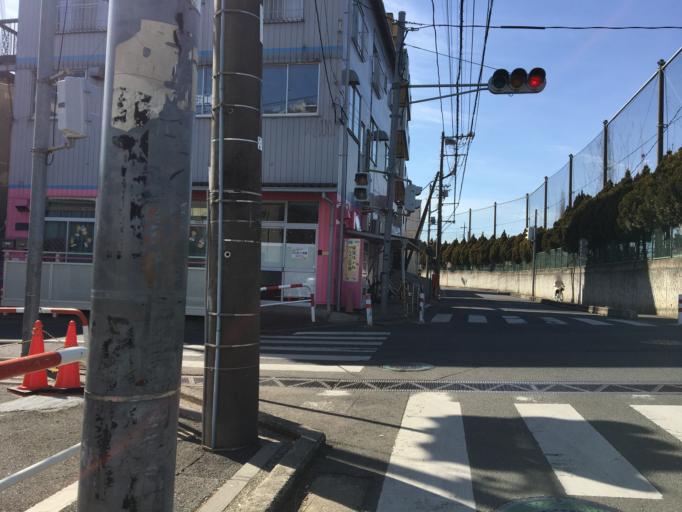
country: JP
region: Saitama
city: Oi
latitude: 35.8314
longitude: 139.5397
